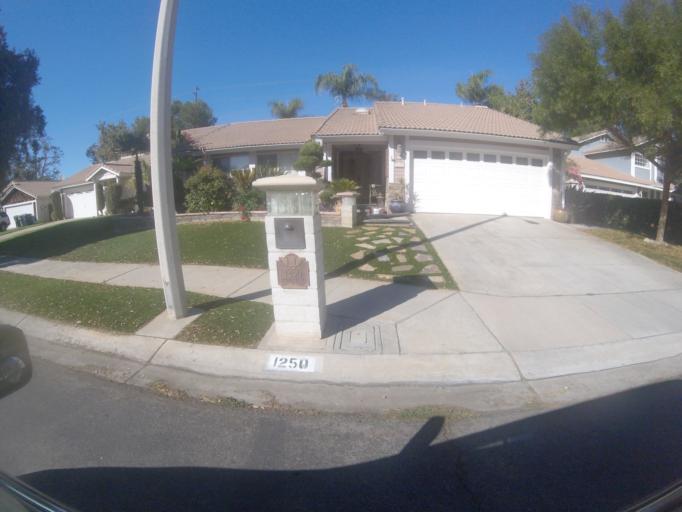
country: US
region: California
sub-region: San Bernardino County
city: Mentone
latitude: 34.0696
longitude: -117.1488
